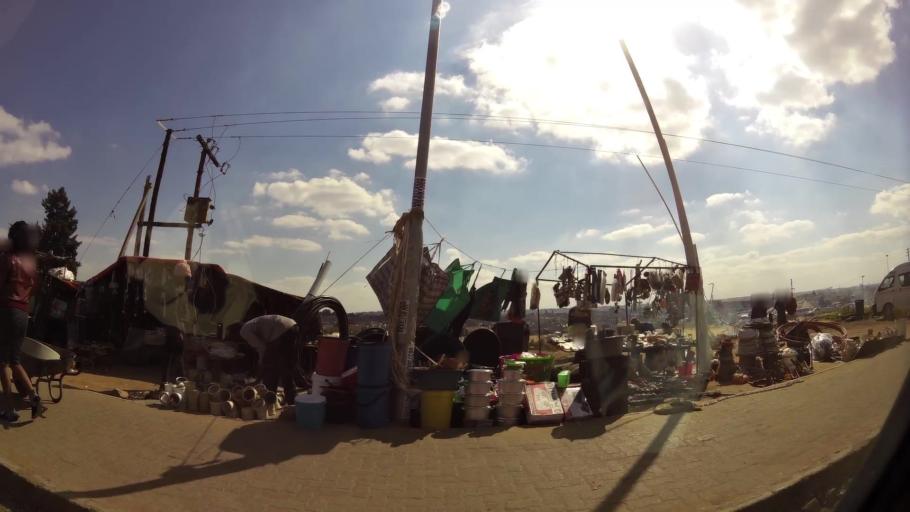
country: ZA
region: Gauteng
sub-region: Ekurhuleni Metropolitan Municipality
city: Tembisa
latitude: -26.0091
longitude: 28.1808
